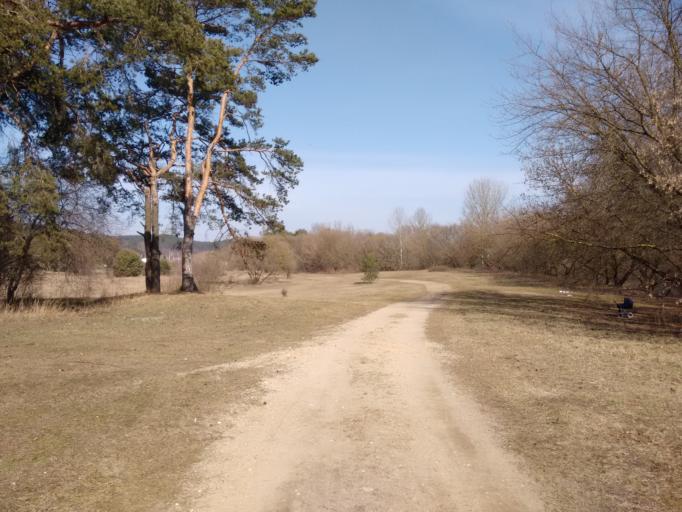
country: LT
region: Vilnius County
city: Vilkpede
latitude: 54.6766
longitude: 25.2305
